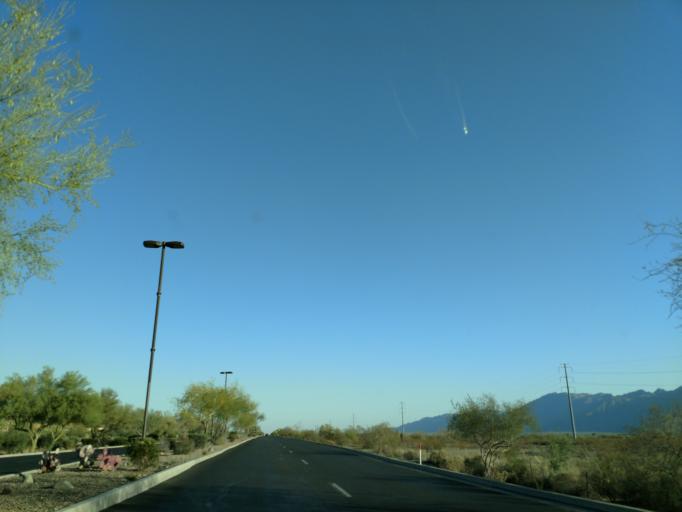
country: US
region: Arizona
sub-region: Maricopa County
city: Laveen
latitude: 33.3157
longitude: -112.1623
